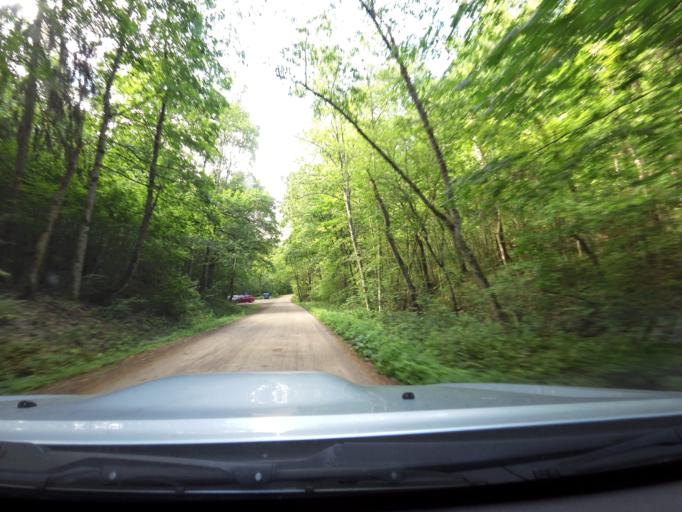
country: LT
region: Vilnius County
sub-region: Vilniaus Rajonas
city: Vievis
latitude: 54.8162
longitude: 24.9653
